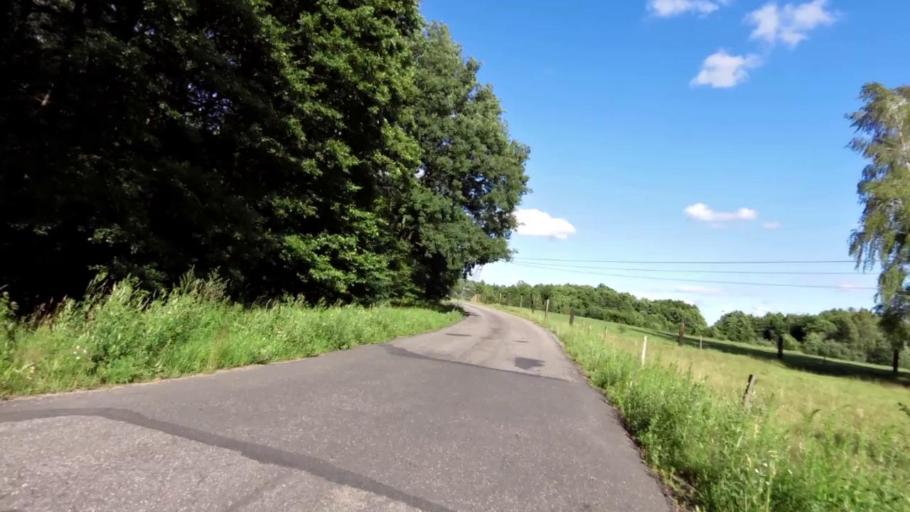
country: PL
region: West Pomeranian Voivodeship
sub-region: Powiat slawienski
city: Slawno
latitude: 54.4360
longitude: 16.7615
